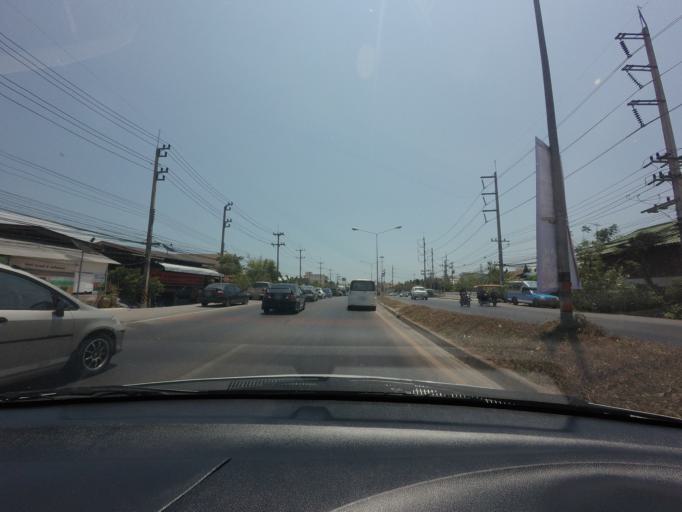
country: TH
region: Samut Songkhram
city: Amphawa
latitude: 13.4205
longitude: 99.9633
